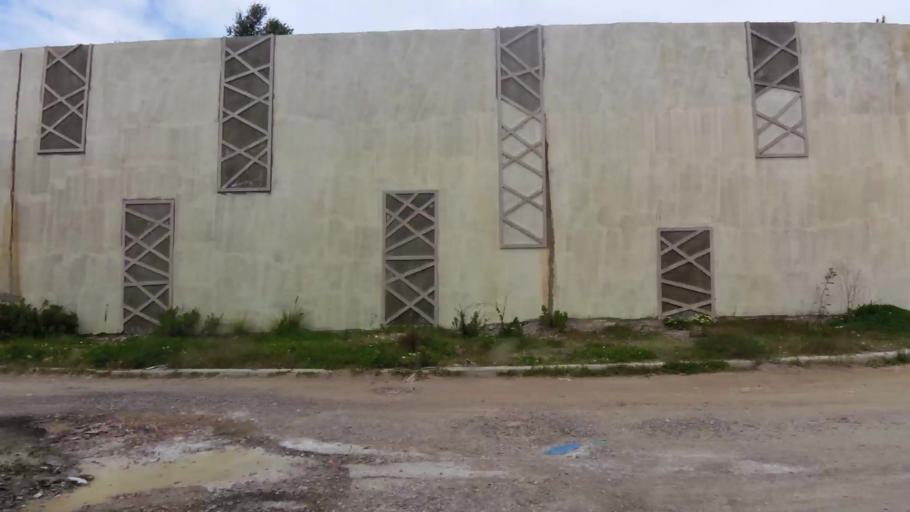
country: MA
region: Tanger-Tetouan
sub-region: Tanger-Assilah
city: Tangier
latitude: 35.7807
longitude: -5.8545
